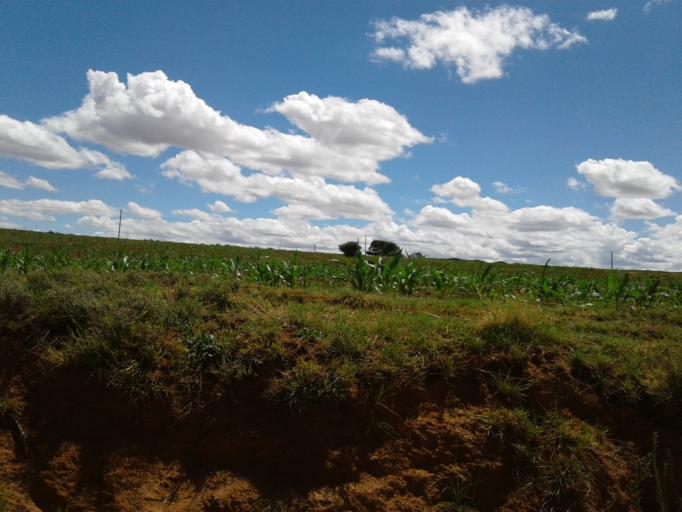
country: LS
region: Quthing
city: Quthing
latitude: -30.3839
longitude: 27.5550
